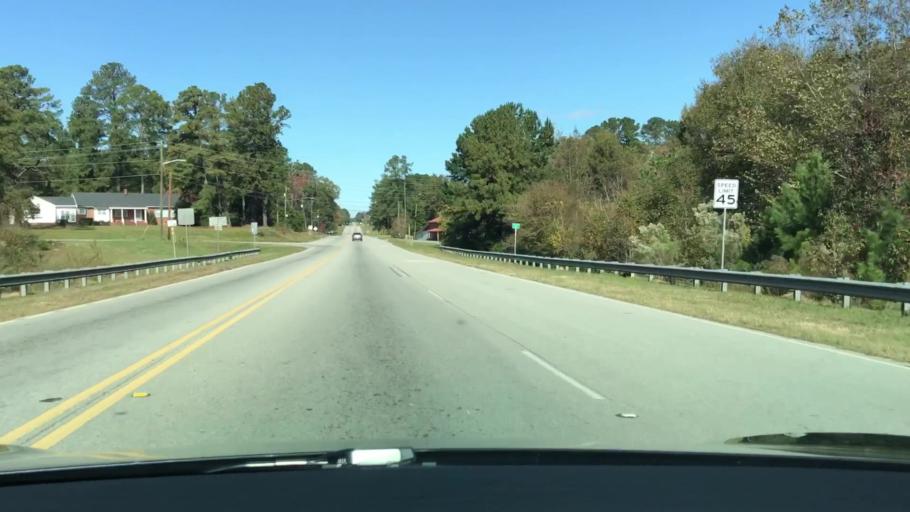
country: US
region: Georgia
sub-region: Warren County
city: West Warrenton
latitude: 33.4071
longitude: -82.6725
